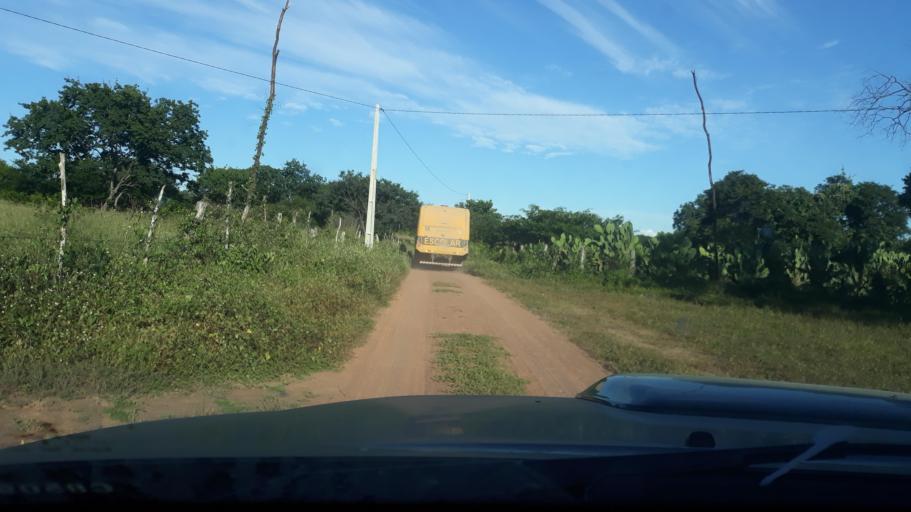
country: BR
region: Bahia
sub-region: Riacho De Santana
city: Riacho de Santana
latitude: -13.8602
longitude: -43.0339
